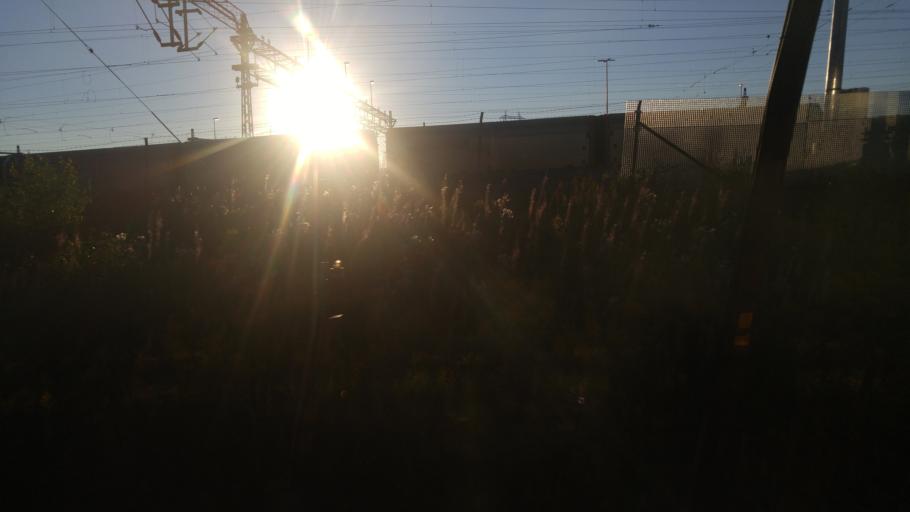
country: NO
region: Oslo
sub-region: Oslo
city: Oslo
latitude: 59.9291
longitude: 10.8337
